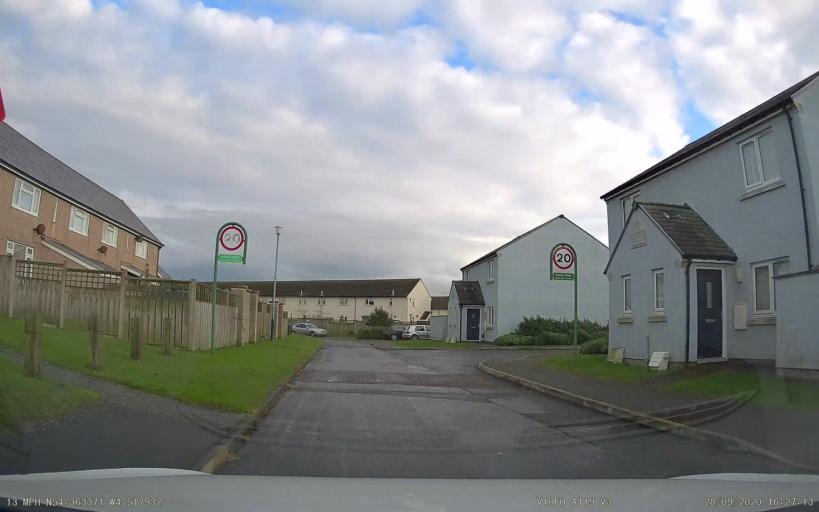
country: IM
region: Ramsey
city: Ramsey
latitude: 54.3633
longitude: -4.5179
